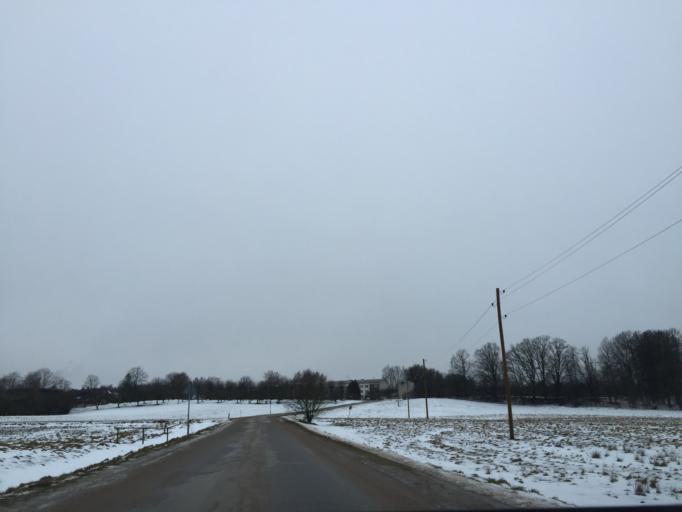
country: LV
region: Krimulda
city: Ragana
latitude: 57.1557
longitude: 24.7079
